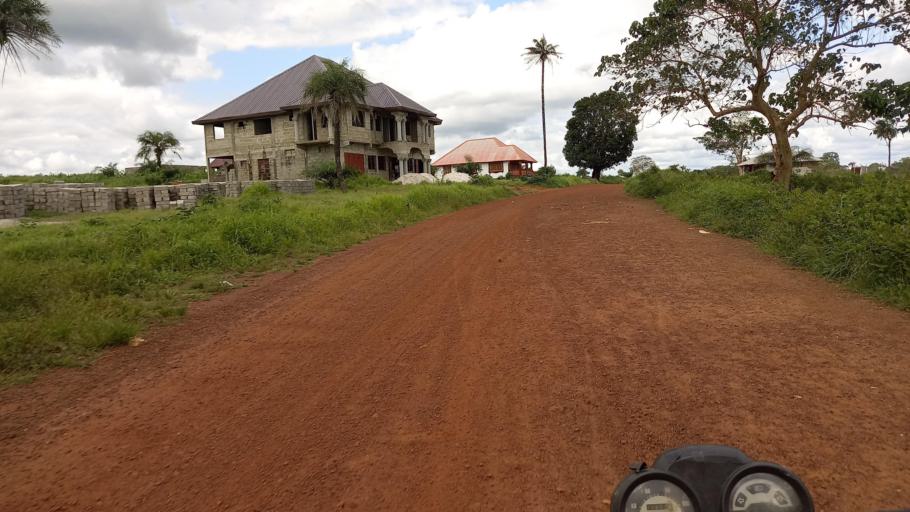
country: SL
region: Northern Province
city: Kamakwie
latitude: 9.5056
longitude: -12.2323
